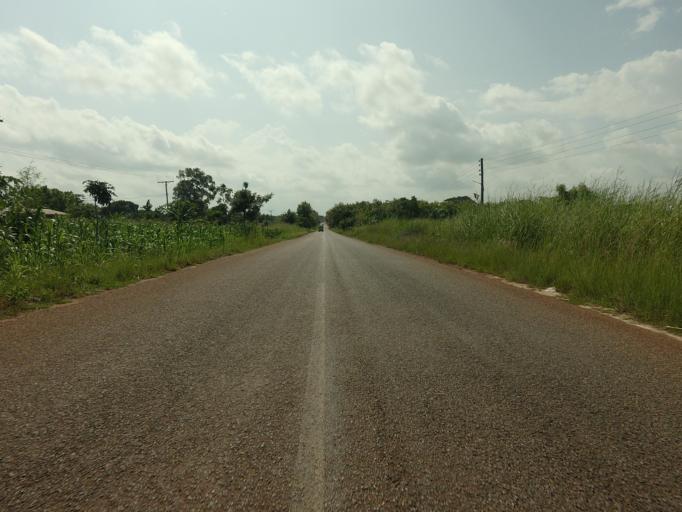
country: TG
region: Maritime
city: Tsevie
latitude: 6.3563
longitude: 0.8685
